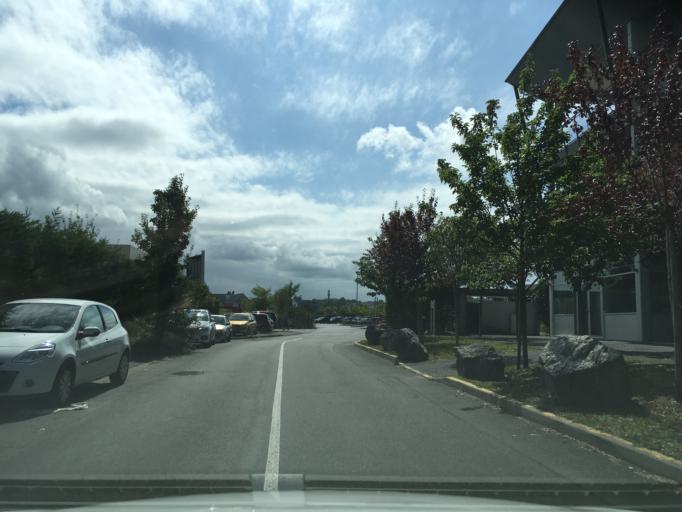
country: FR
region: Aquitaine
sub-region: Departement des Pyrenees-Atlantiques
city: Bayonne
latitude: 43.4929
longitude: -1.4518
